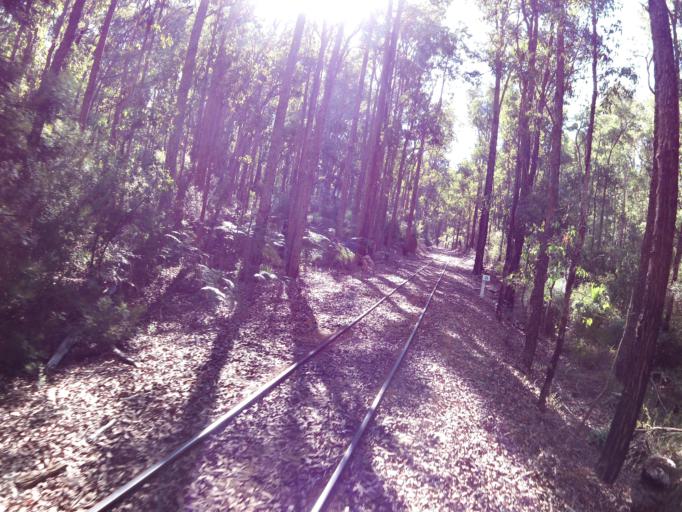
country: AU
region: Western Australia
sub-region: Waroona
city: Waroona
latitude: -32.7248
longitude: 116.1094
